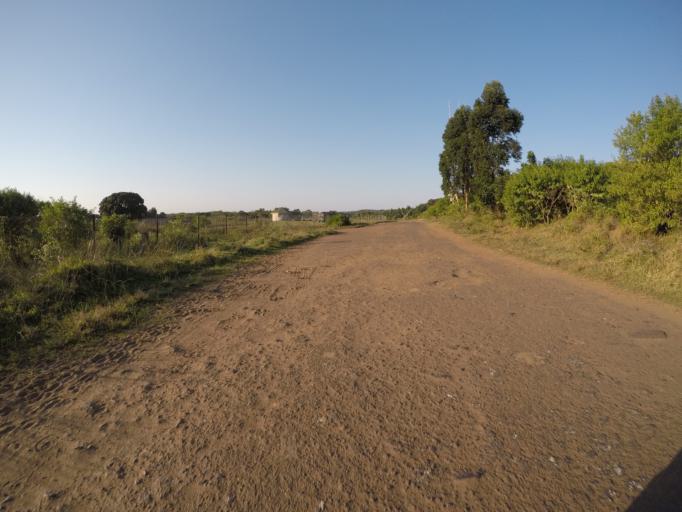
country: ZA
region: KwaZulu-Natal
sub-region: uThungulu District Municipality
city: KwaMbonambi
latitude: -28.6934
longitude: 32.1992
